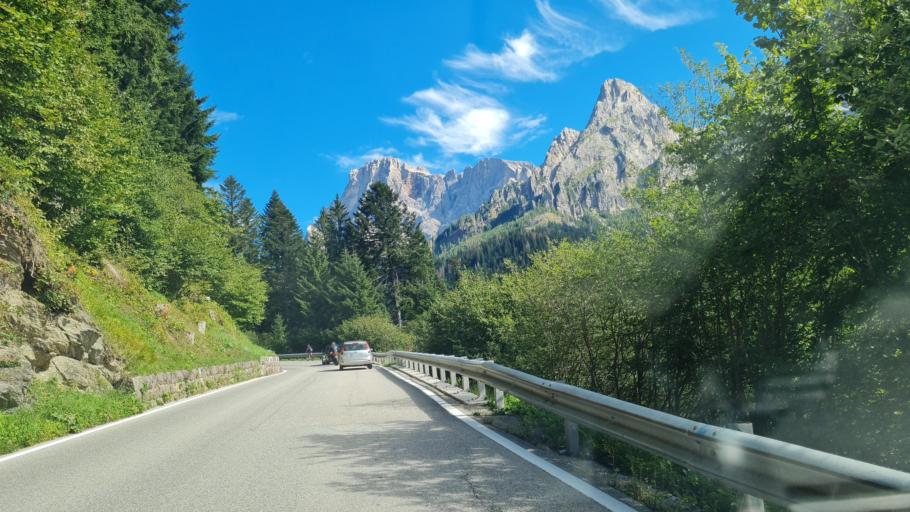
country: IT
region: Trentino-Alto Adige
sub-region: Provincia di Trento
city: Siror
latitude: 46.2358
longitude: 11.8072
